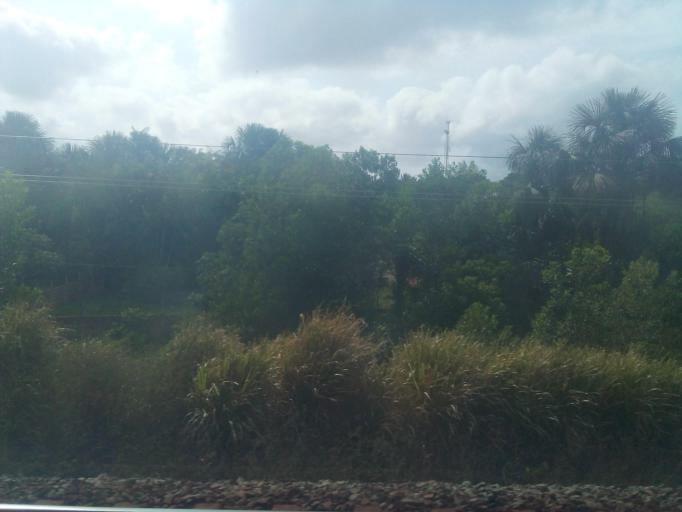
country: BR
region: Maranhao
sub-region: Sao Luis
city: Sao Luis
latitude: -2.7296
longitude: -44.3356
